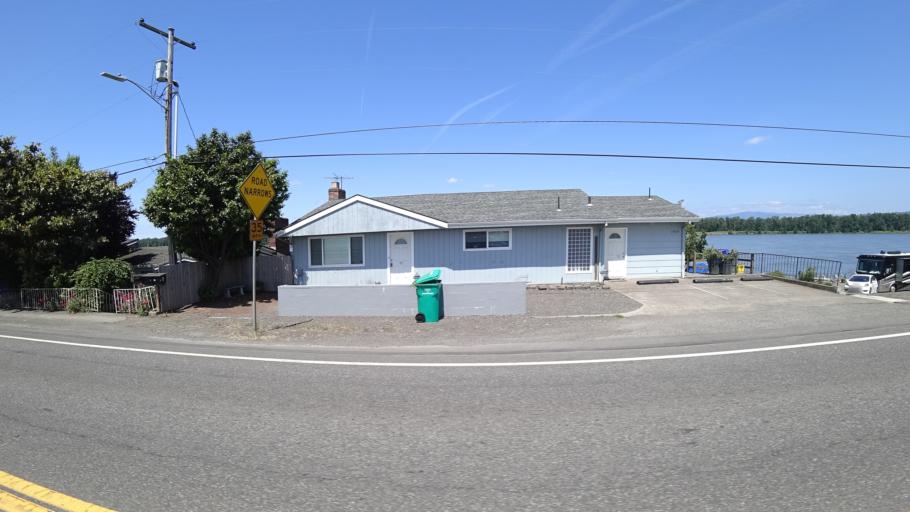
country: US
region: Washington
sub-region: Clark County
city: Mill Plain
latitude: 45.5649
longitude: -122.5195
